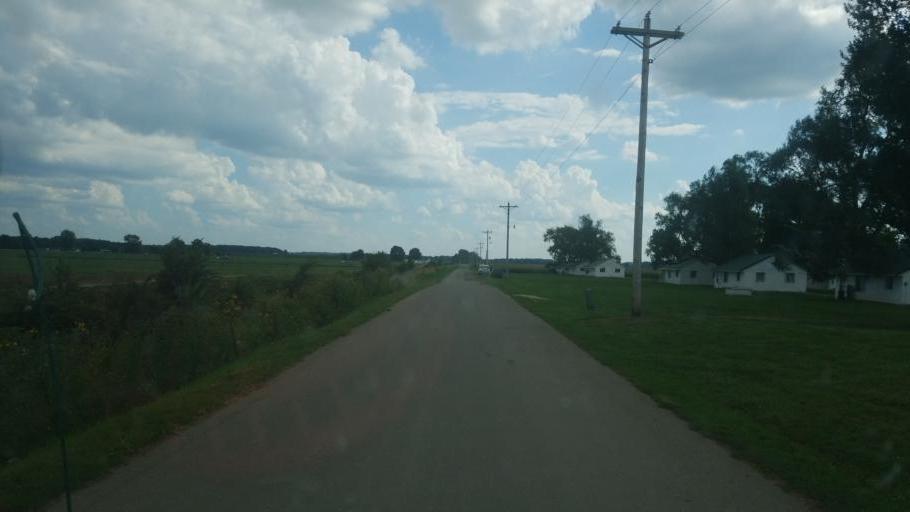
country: US
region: Ohio
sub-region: Huron County
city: Willard
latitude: 41.0031
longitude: -82.7393
